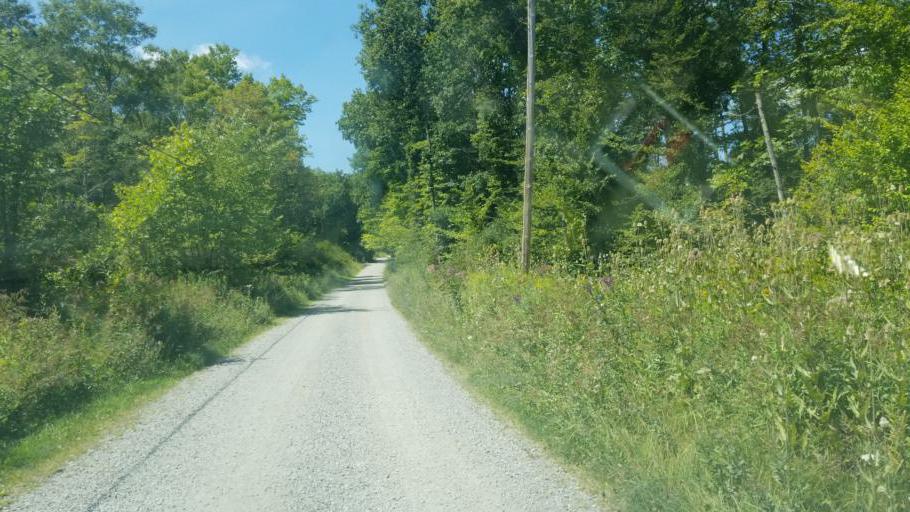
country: US
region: Pennsylvania
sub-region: Clarion County
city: Knox
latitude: 41.2040
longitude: -79.6342
